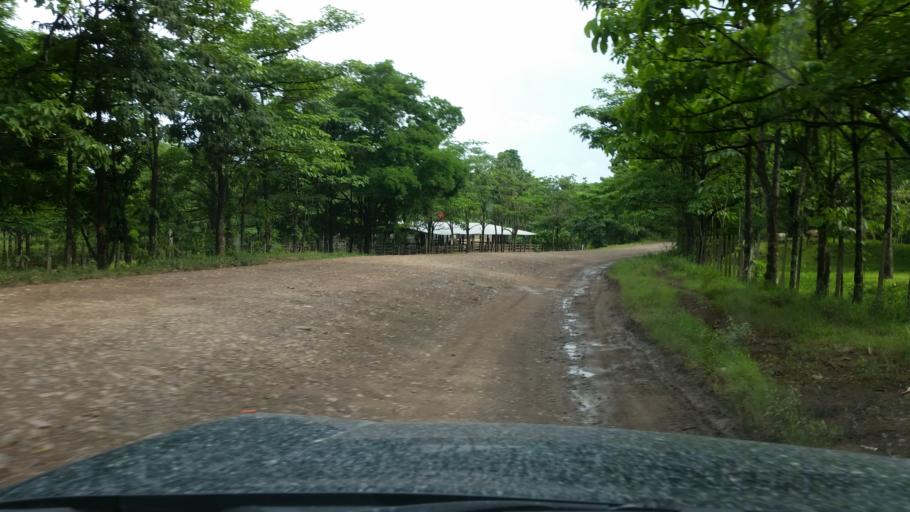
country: NI
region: Atlantico Norte (RAAN)
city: Siuna
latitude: 13.4579
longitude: -84.8496
